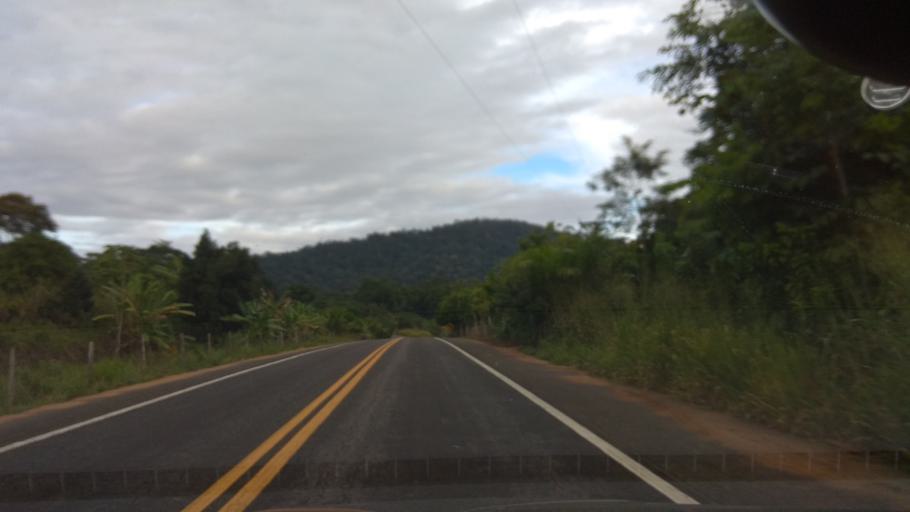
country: BR
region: Bahia
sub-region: Ubaitaba
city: Ubaitaba
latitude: -14.2561
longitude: -39.3538
